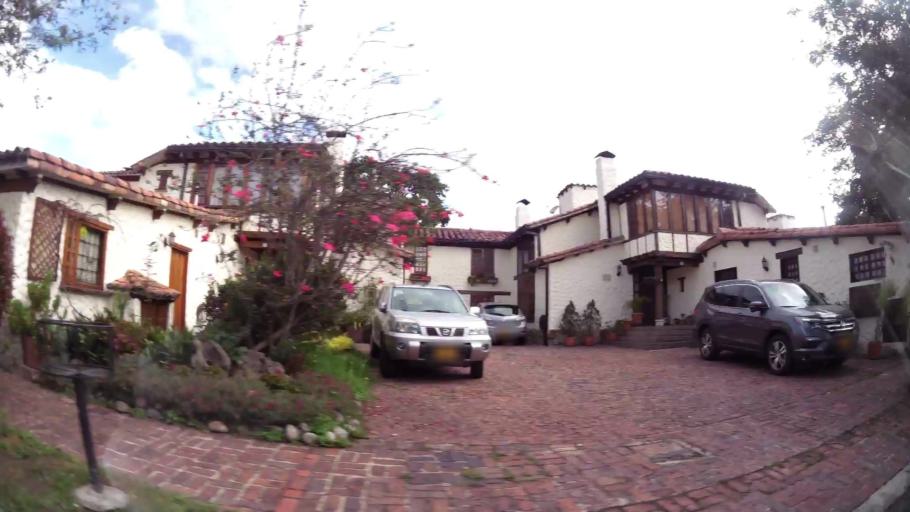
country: CO
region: Bogota D.C.
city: Barrio San Luis
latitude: 4.7153
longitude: -74.0740
